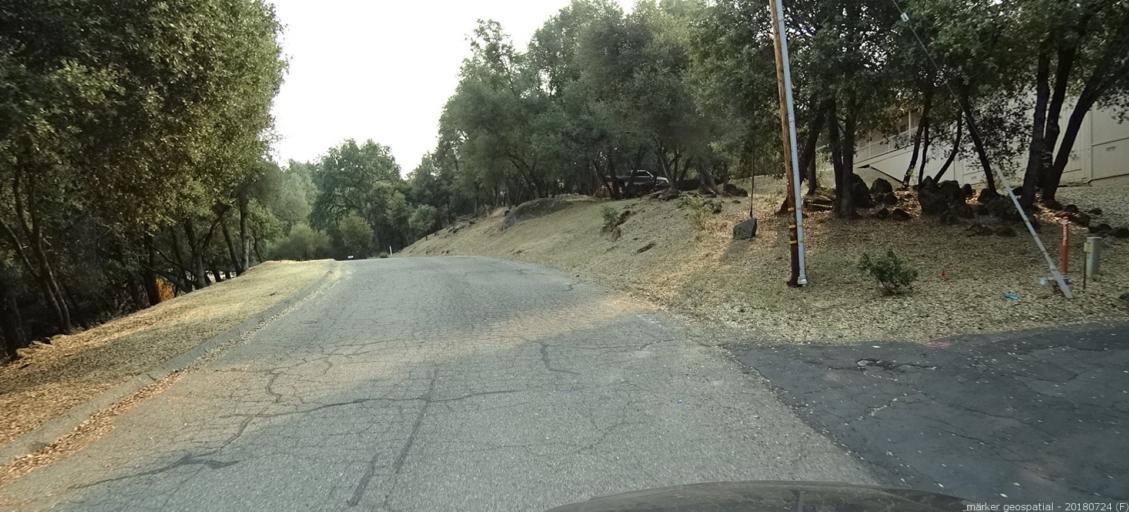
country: US
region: California
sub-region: Madera County
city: Oakhurst
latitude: 37.3198
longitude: -119.6227
